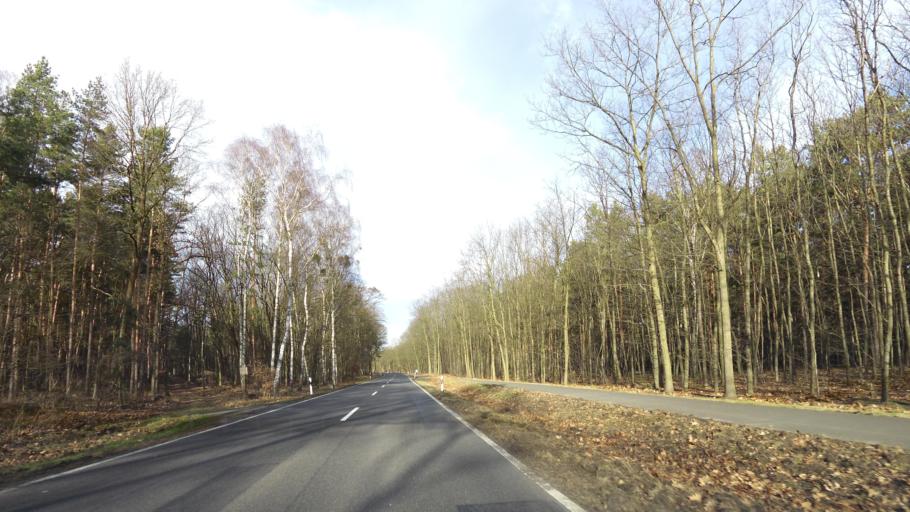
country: DE
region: Brandenburg
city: Michendorf
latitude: 52.3286
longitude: 13.0248
